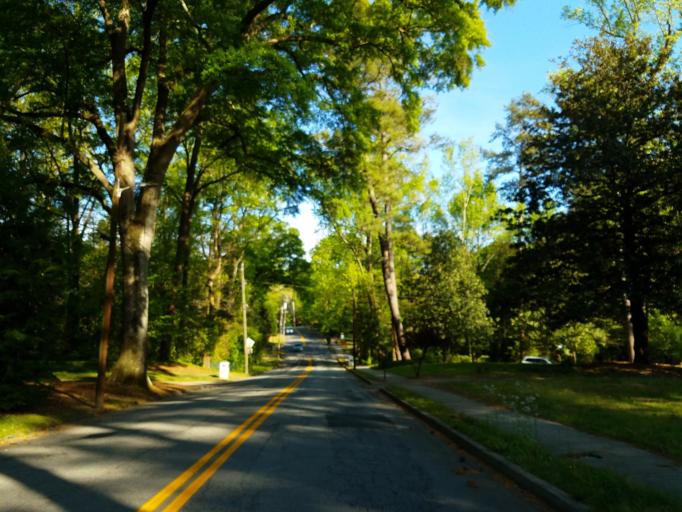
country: US
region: Georgia
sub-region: Cobb County
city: Vinings
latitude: 33.8255
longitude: -84.4216
